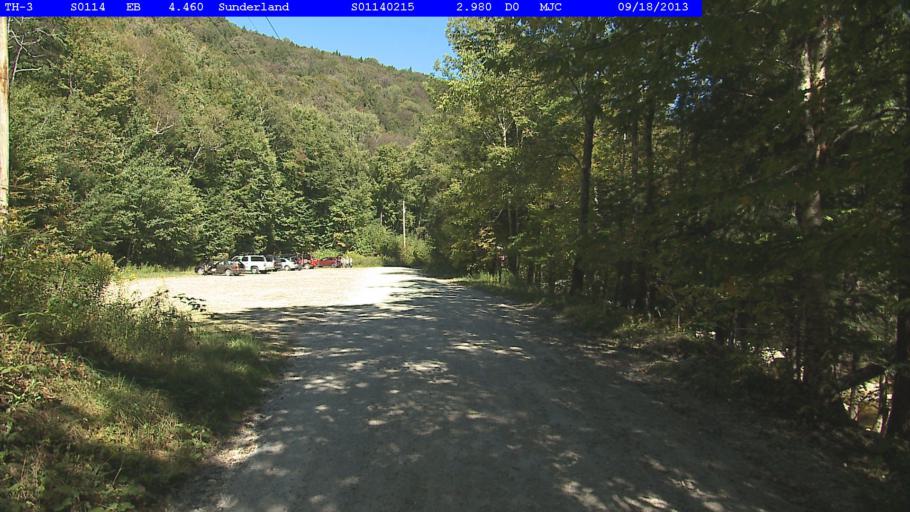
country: US
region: Vermont
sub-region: Bennington County
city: Arlington
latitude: 43.0427
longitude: -73.1027
